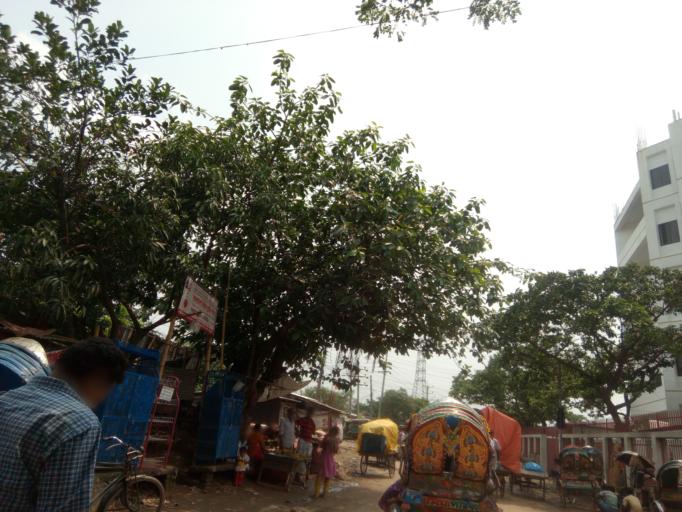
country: BD
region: Dhaka
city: Azimpur
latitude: 23.7147
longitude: 90.3834
